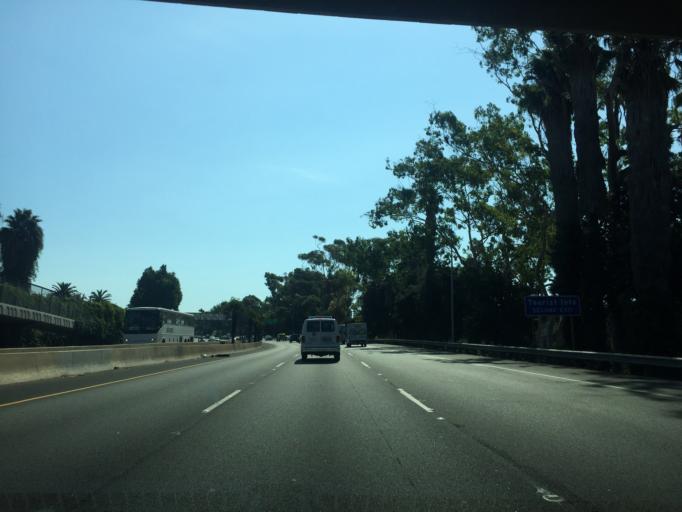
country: US
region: California
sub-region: Santa Barbara County
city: Santa Barbara
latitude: 34.4144
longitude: -119.7050
